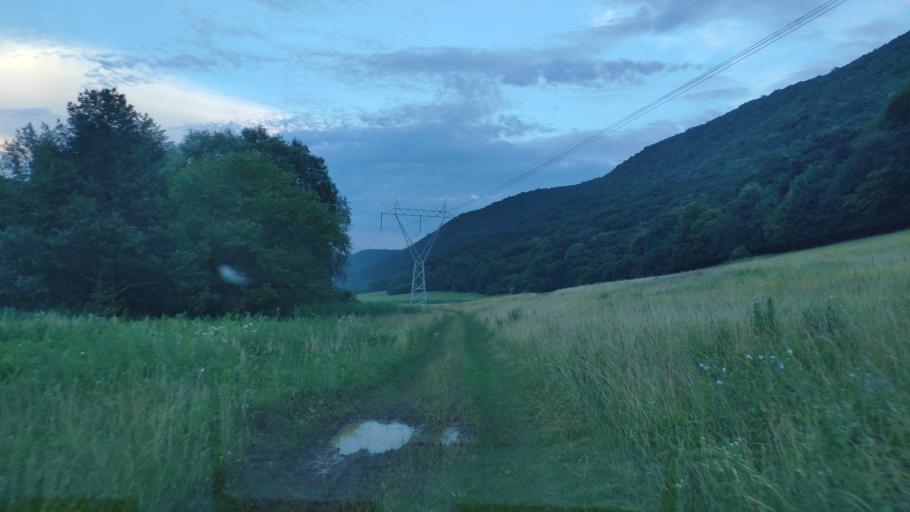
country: SK
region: Kosicky
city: Medzev
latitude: 48.5848
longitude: 20.7561
